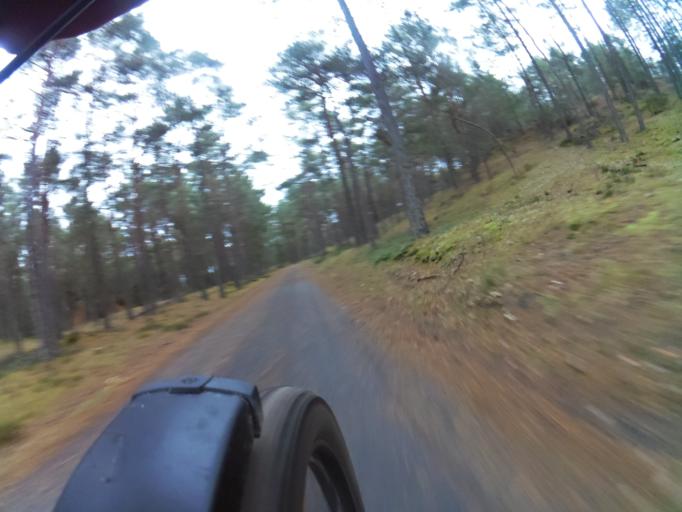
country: PL
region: Pomeranian Voivodeship
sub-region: Powiat wejherowski
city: Choczewo
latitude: 54.7852
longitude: 17.7460
